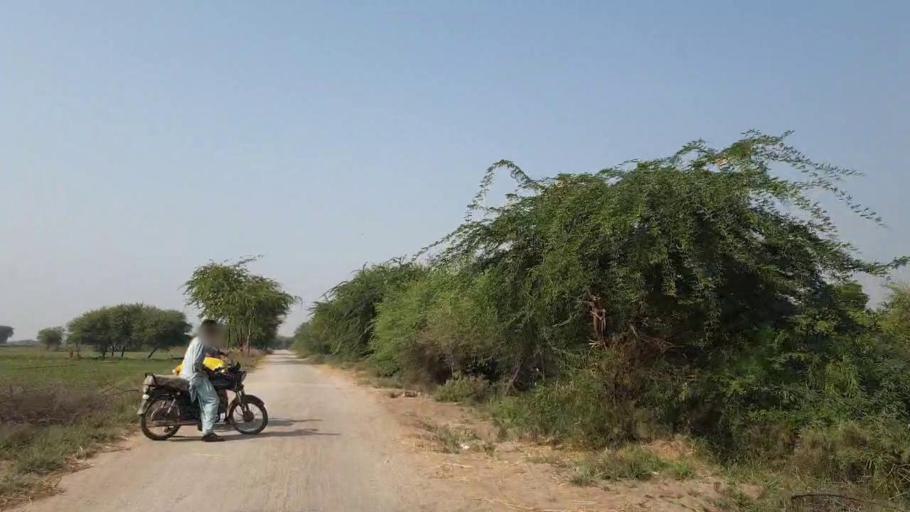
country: PK
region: Sindh
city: Kario
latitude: 24.9409
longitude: 68.5370
